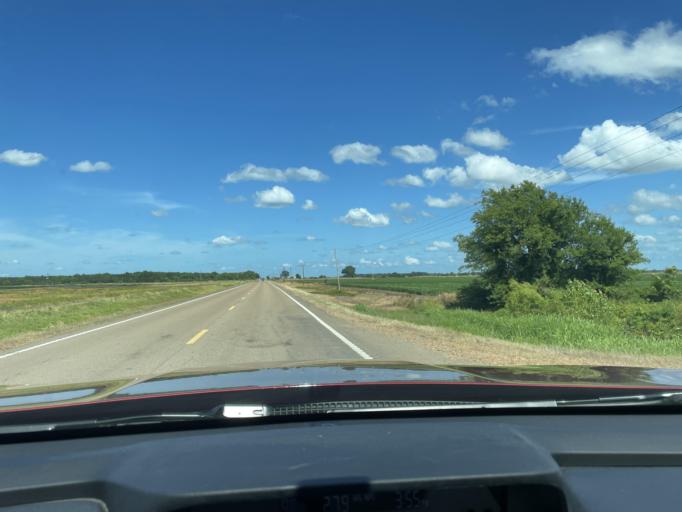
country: US
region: Mississippi
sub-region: Humphreys County
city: Belzoni
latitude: 33.1827
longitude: -90.6417
